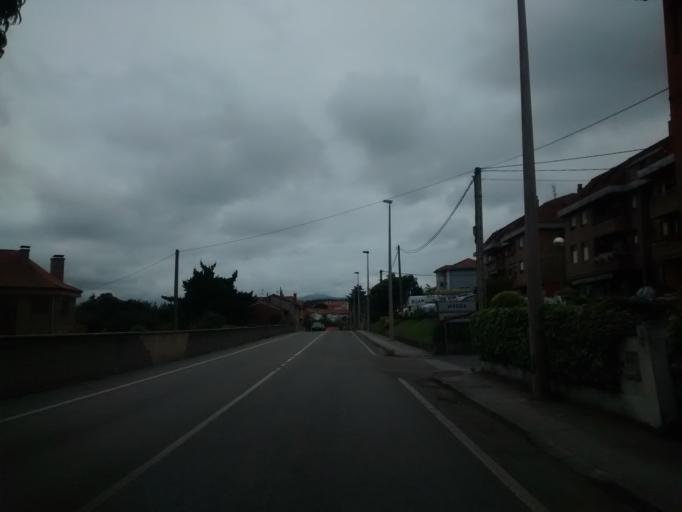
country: ES
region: Cantabria
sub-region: Provincia de Cantabria
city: Polanco
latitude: 43.3839
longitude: -4.0479
